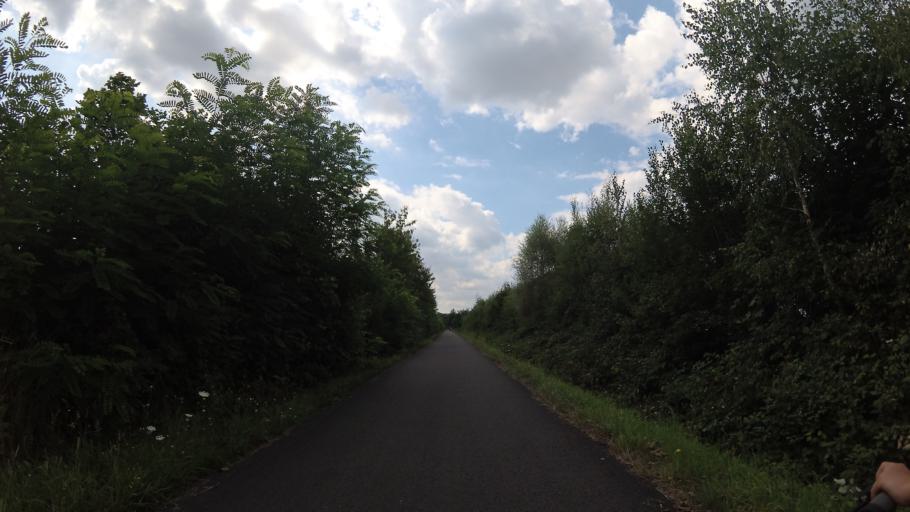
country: DE
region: Saarland
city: Blieskastel
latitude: 49.2318
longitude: 7.2598
